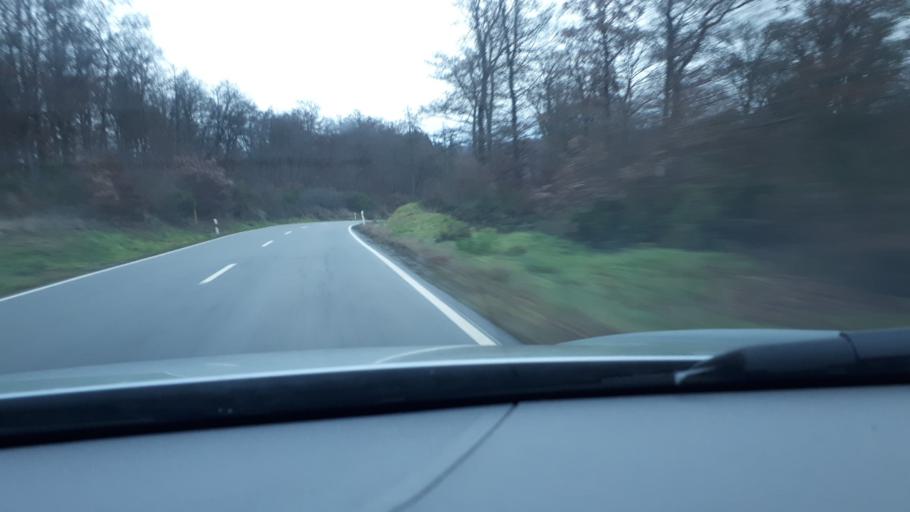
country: DE
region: Rheinland-Pfalz
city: Dungenheim
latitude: 50.2649
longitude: 7.1915
